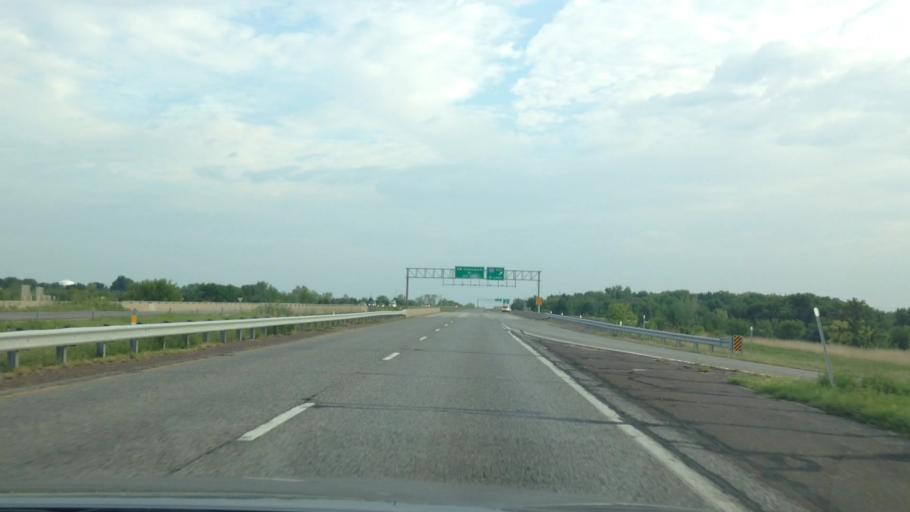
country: US
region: Missouri
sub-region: Clay County
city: Smithville
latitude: 39.3110
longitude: -94.5846
